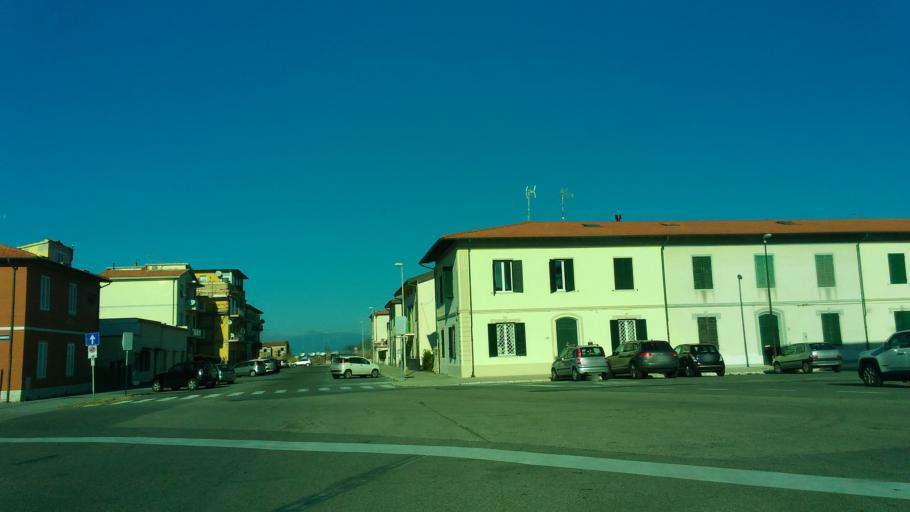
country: IT
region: Tuscany
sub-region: Province of Pisa
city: Marina di Pisa
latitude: 43.6749
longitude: 10.2742
